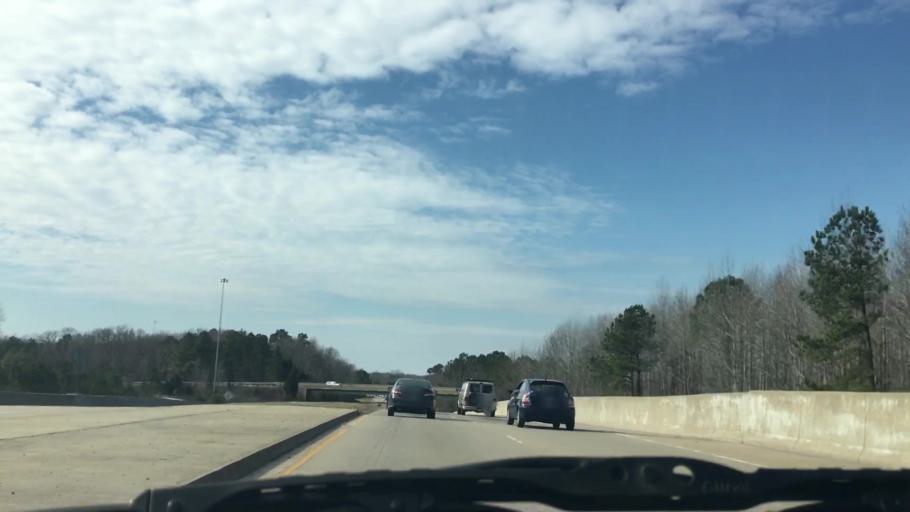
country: US
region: Virginia
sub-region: City of Portsmouth
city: Portsmouth Heights
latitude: 36.8654
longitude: -76.4274
